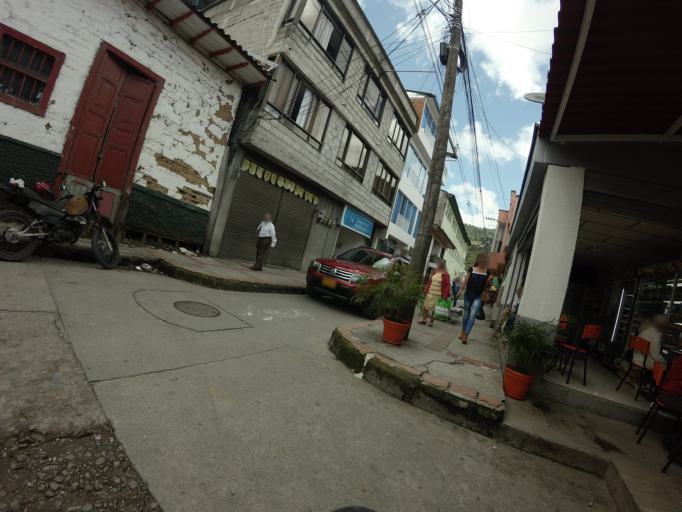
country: CO
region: Caldas
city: Manzanares
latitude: 5.2529
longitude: -75.1538
